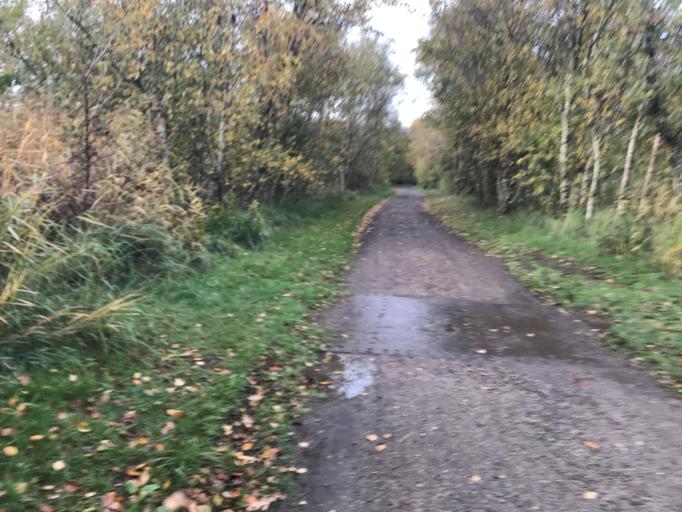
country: DE
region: Lower Saxony
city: Borkum
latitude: 53.5748
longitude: 6.7074
